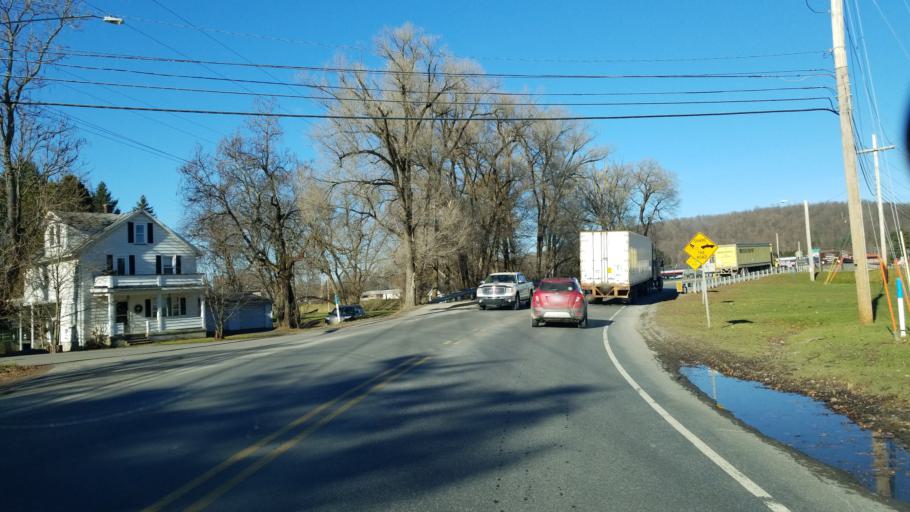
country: US
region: Pennsylvania
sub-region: Jefferson County
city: Brockway
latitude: 41.2438
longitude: -78.7876
